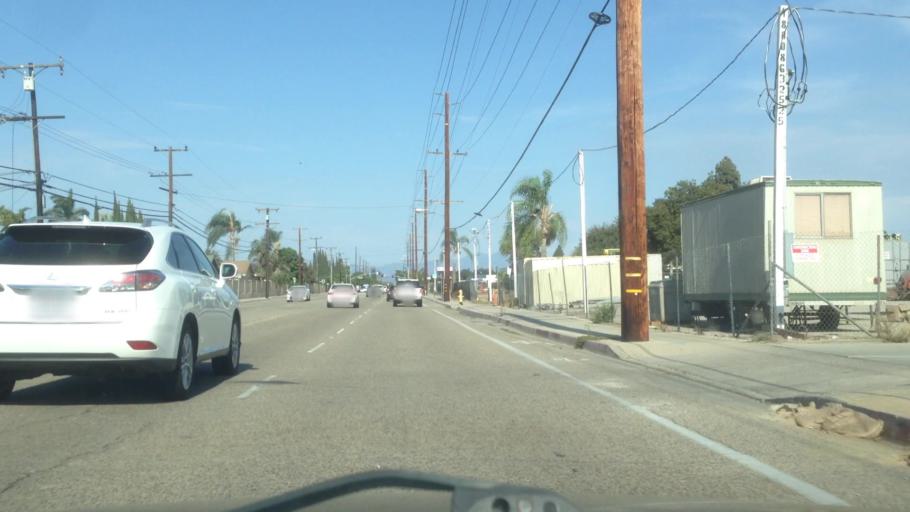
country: US
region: California
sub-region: Orange County
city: Fountain Valley
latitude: 33.7378
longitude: -117.9502
